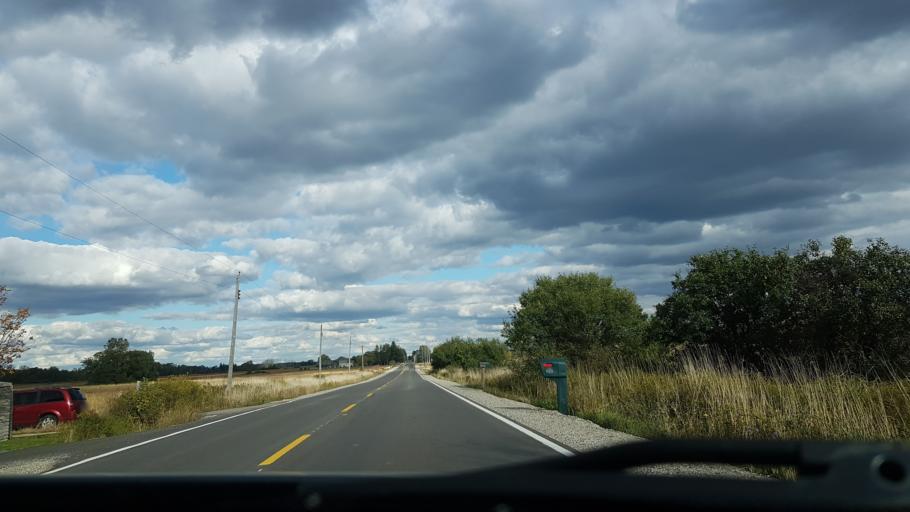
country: CA
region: Ontario
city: London
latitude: 43.0238
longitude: -81.3383
